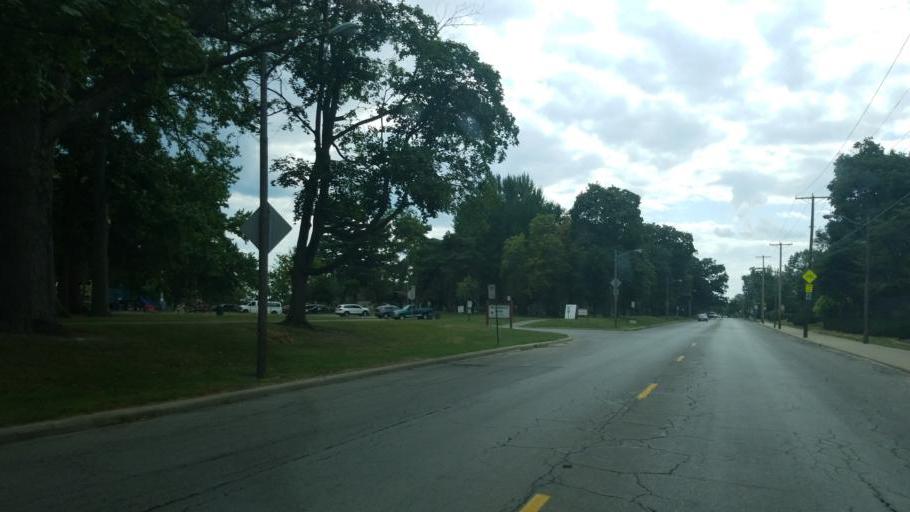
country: US
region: Ohio
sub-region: Wood County
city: Rossford
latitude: 41.6166
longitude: -83.5809
